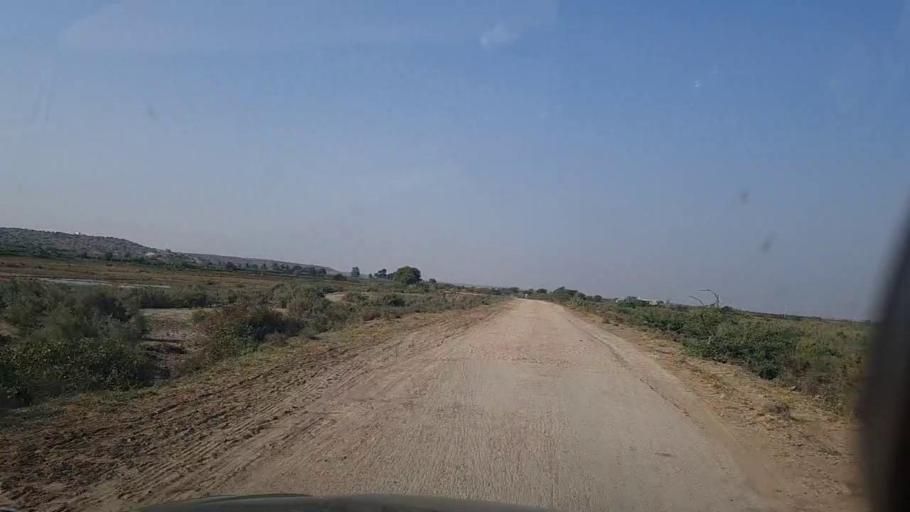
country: PK
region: Sindh
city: Thatta
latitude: 24.5922
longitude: 67.8757
